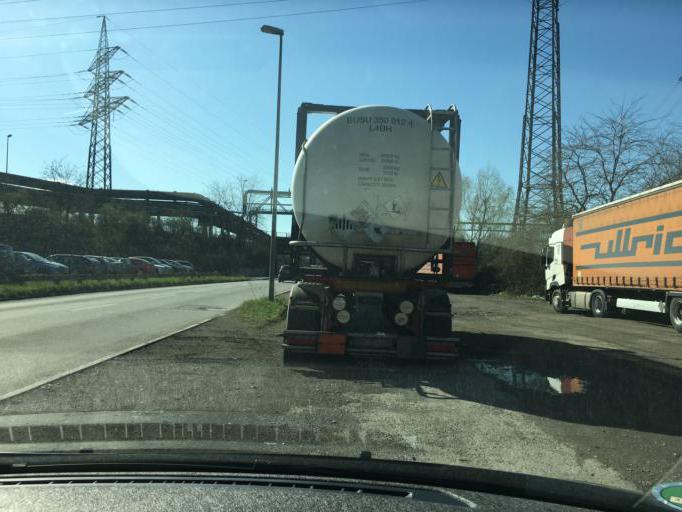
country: DE
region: North Rhine-Westphalia
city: Meiderich
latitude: 51.4886
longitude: 6.7254
